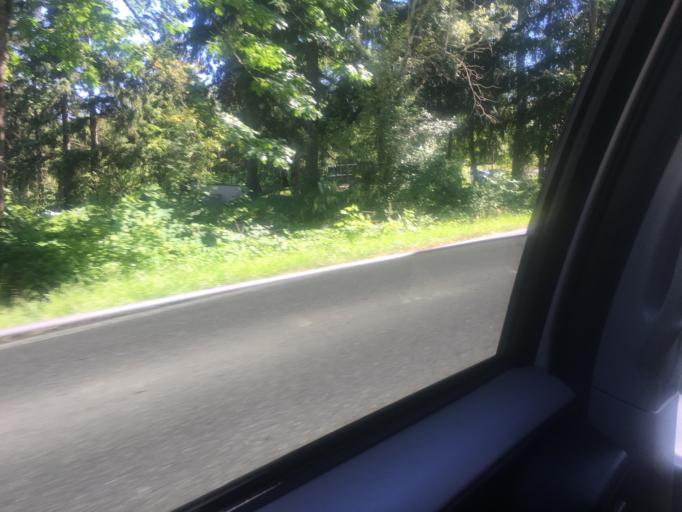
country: US
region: Washington
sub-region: King County
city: Bellevue
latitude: 47.6100
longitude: -122.1806
